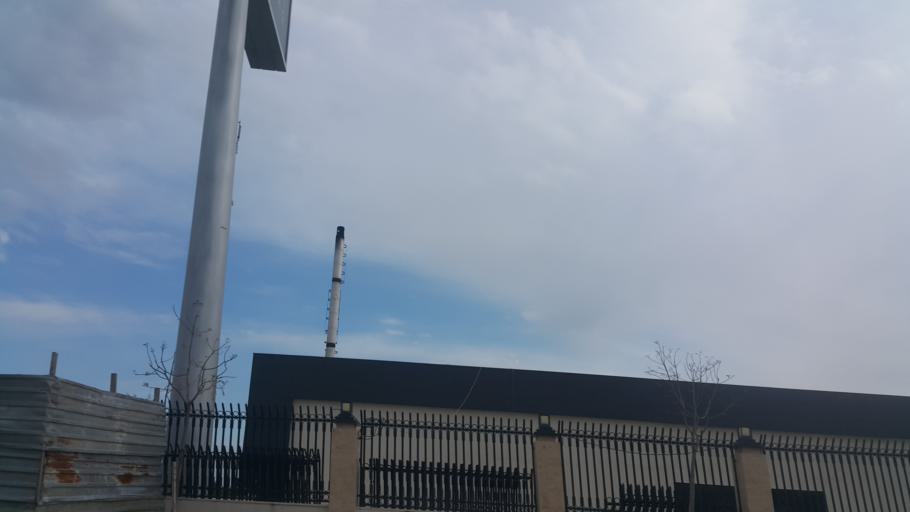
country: TR
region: Mersin
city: Yenice
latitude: 36.9914
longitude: 35.1713
